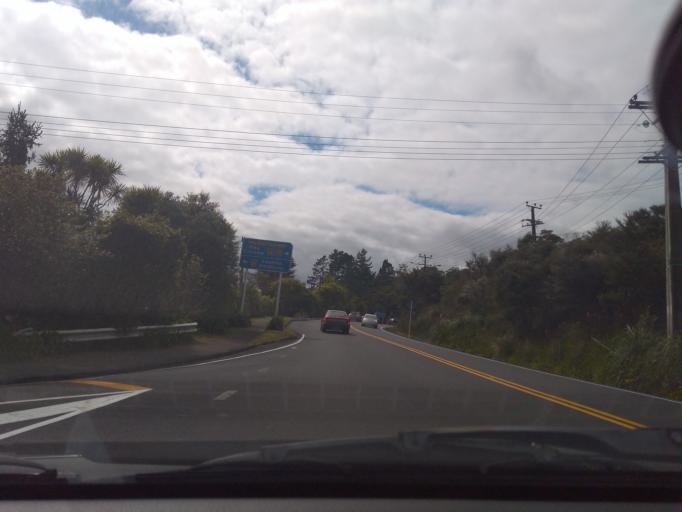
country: NZ
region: Auckland
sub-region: Auckland
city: Rosebank
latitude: -36.8647
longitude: 174.5654
